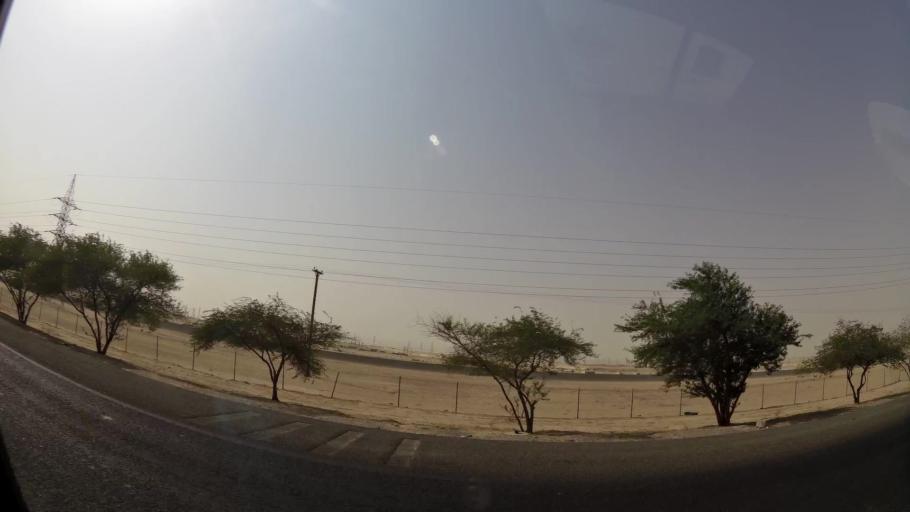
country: KW
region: Muhafazat al Jahra'
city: Al Jahra'
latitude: 29.3201
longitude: 47.6428
